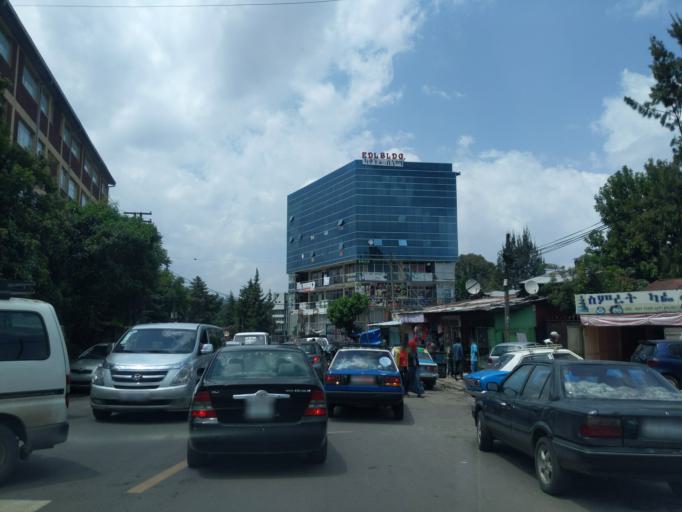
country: ET
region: Adis Abeba
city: Addis Ababa
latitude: 9.0165
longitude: 38.7726
